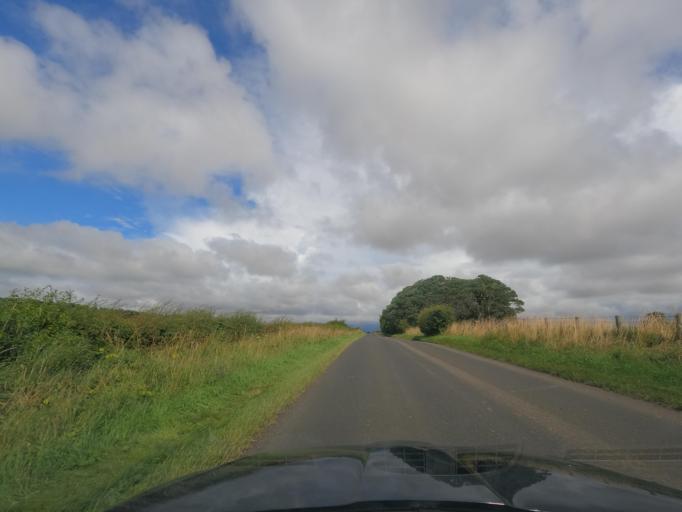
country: GB
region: England
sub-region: Northumberland
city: Lowick
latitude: 55.6410
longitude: -1.9935
